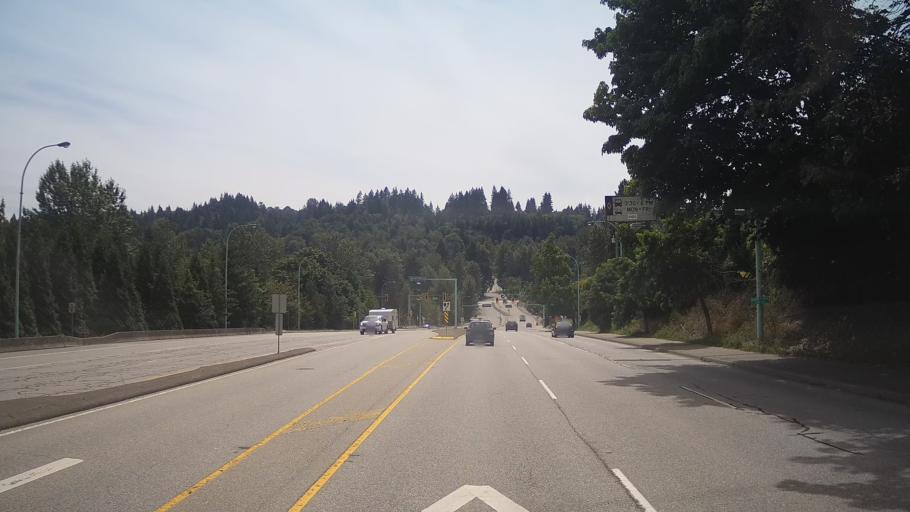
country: CA
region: British Columbia
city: Port Moody
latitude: 49.2812
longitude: -122.8669
